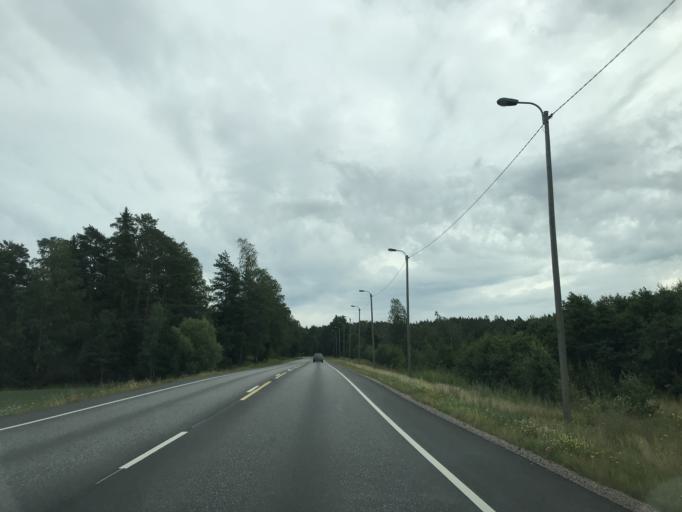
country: FI
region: Varsinais-Suomi
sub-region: Turku
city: Paimio
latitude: 60.4192
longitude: 22.6716
